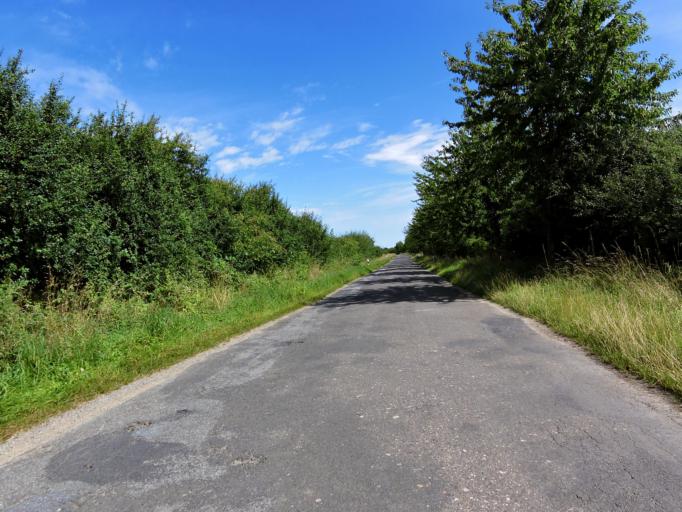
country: DE
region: Mecklenburg-Vorpommern
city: Loitz
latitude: 53.3149
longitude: 13.4014
